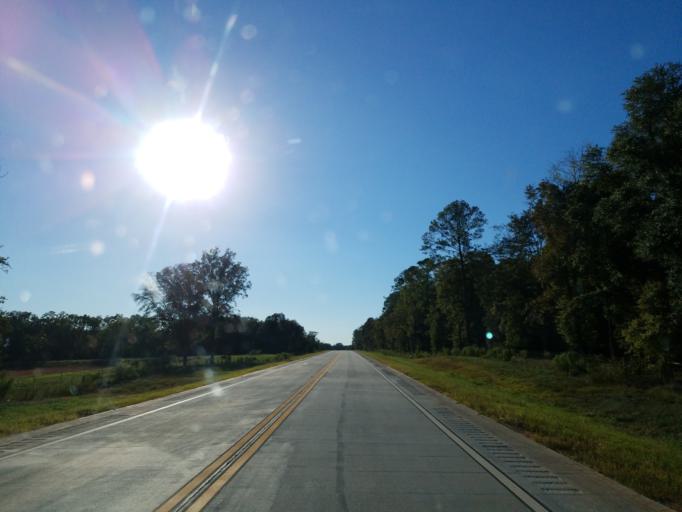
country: US
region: Georgia
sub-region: Lee County
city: Leesburg
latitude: 31.7501
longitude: -84.1618
